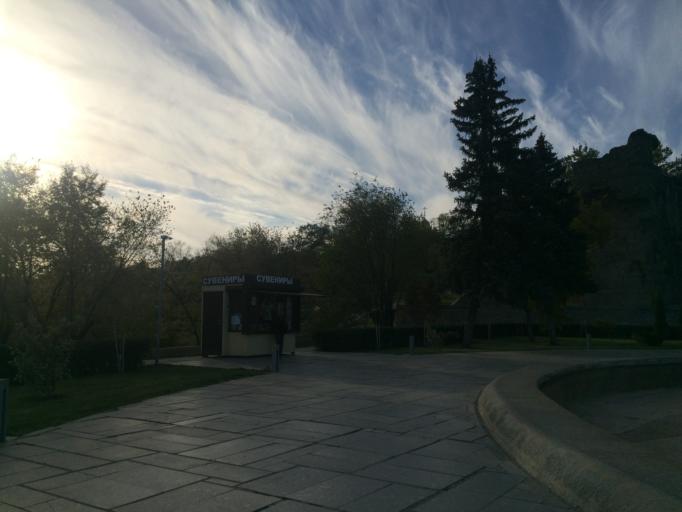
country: RU
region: Volgograd
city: Volgograd
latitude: 48.7406
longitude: 44.5420
